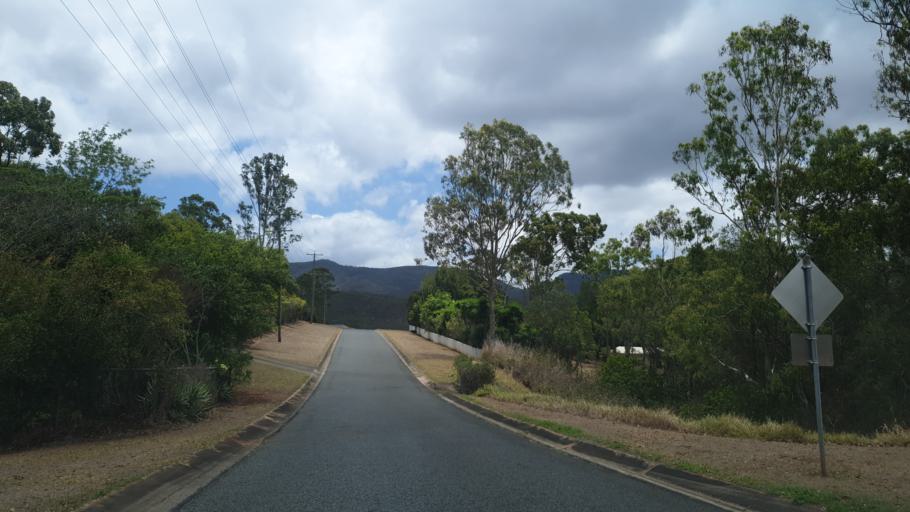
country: AU
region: Queensland
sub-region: Tablelands
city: Tolga
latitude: -17.2097
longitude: 145.4461
